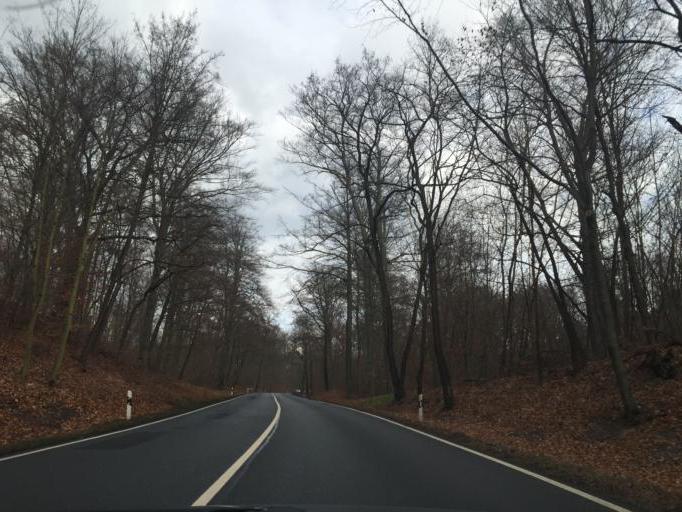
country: DE
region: Saxony
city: Albertstadt
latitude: 51.0770
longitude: 13.8007
